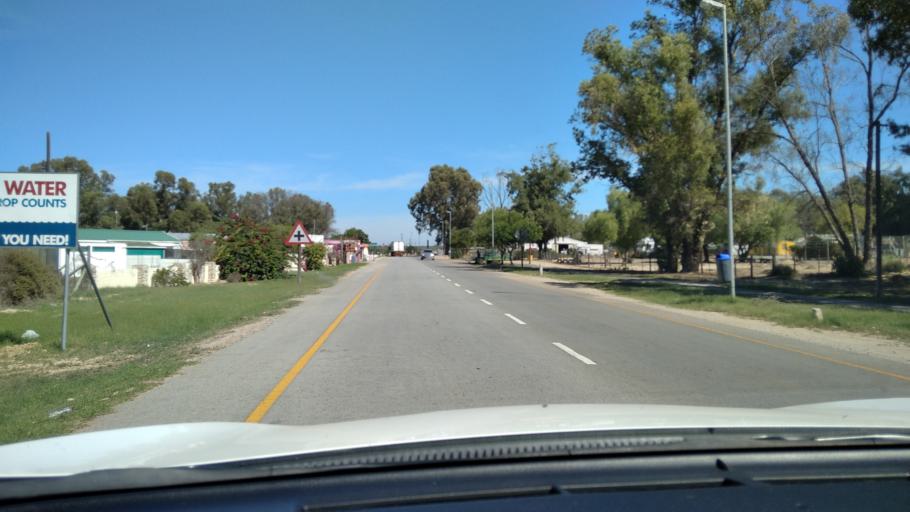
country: ZA
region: Western Cape
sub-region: West Coast District Municipality
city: Moorreesburg
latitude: -33.0582
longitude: 18.3424
